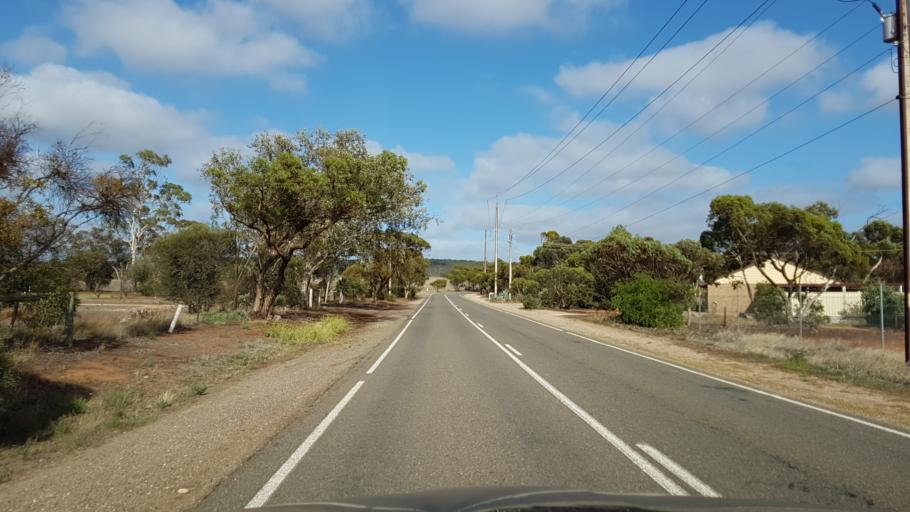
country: AU
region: South Australia
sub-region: Murray Bridge
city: Murray Bridge
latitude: -35.1175
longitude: 139.2423
